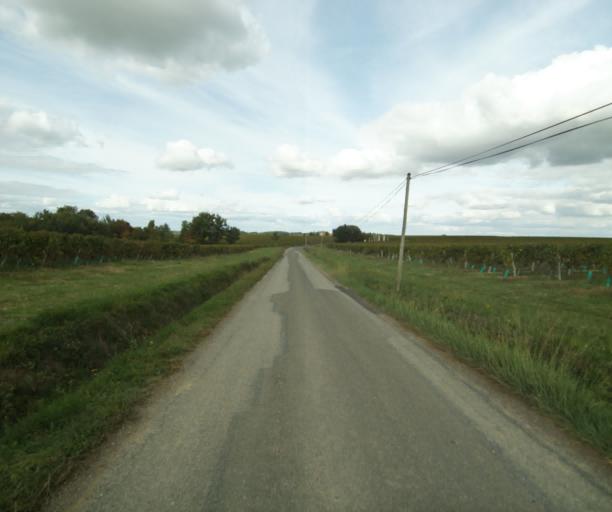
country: FR
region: Midi-Pyrenees
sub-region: Departement du Gers
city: Eauze
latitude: 43.8509
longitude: 0.1596
